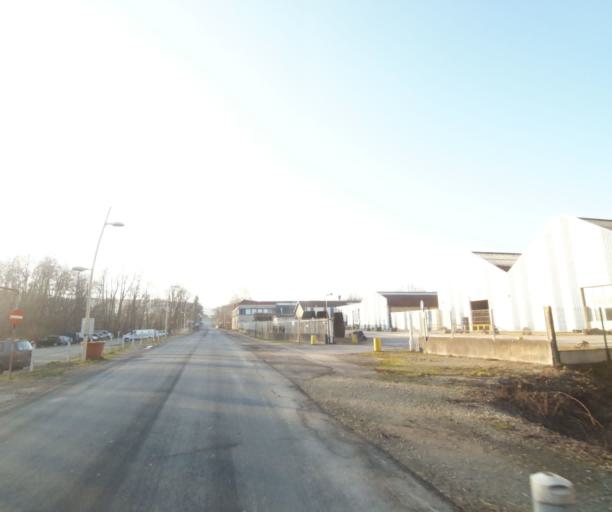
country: FR
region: Champagne-Ardenne
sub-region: Departement de la Haute-Marne
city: Chevillon
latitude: 48.5238
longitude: 5.1082
